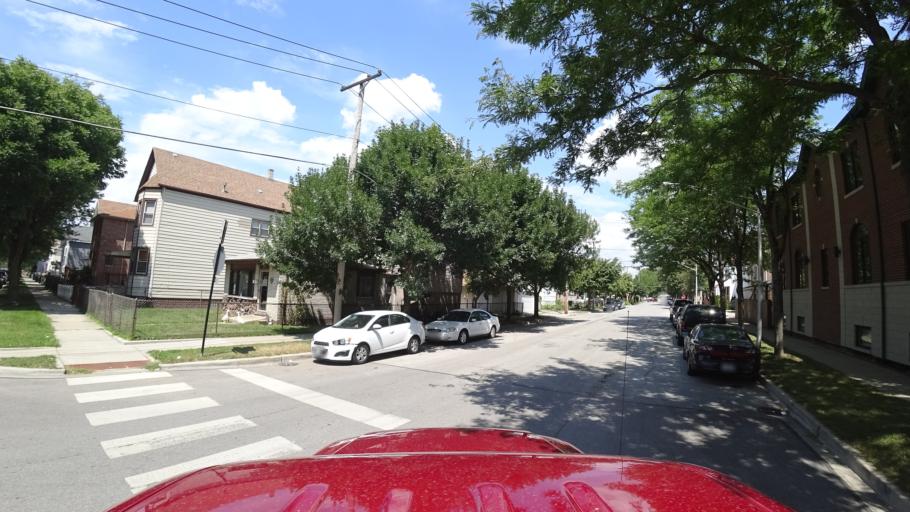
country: US
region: Illinois
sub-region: Cook County
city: Chicago
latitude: 41.8173
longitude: -87.6383
